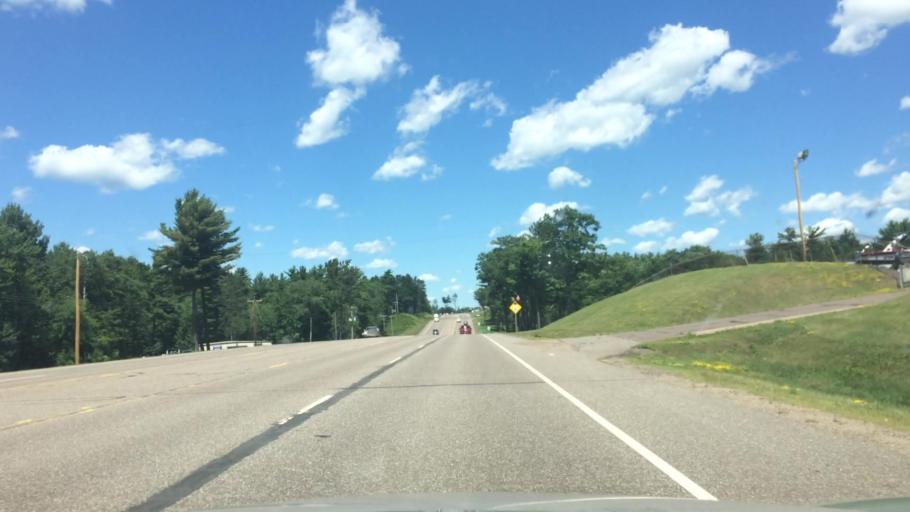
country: US
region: Wisconsin
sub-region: Vilas County
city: Lac du Flambeau
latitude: 45.8441
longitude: -89.7059
